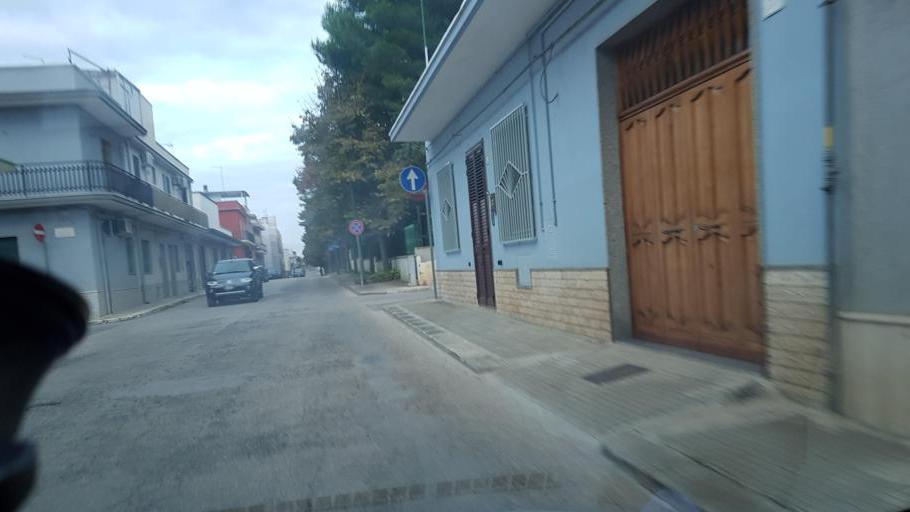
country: IT
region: Apulia
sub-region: Provincia di Brindisi
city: Latiano
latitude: 40.5472
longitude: 17.7173
